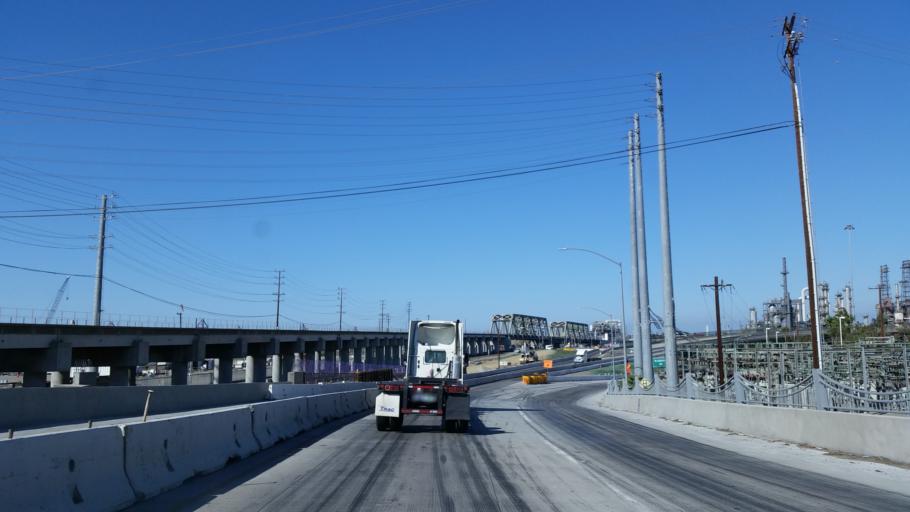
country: US
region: California
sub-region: Los Angeles County
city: Long Beach
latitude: 33.7722
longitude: -118.2403
